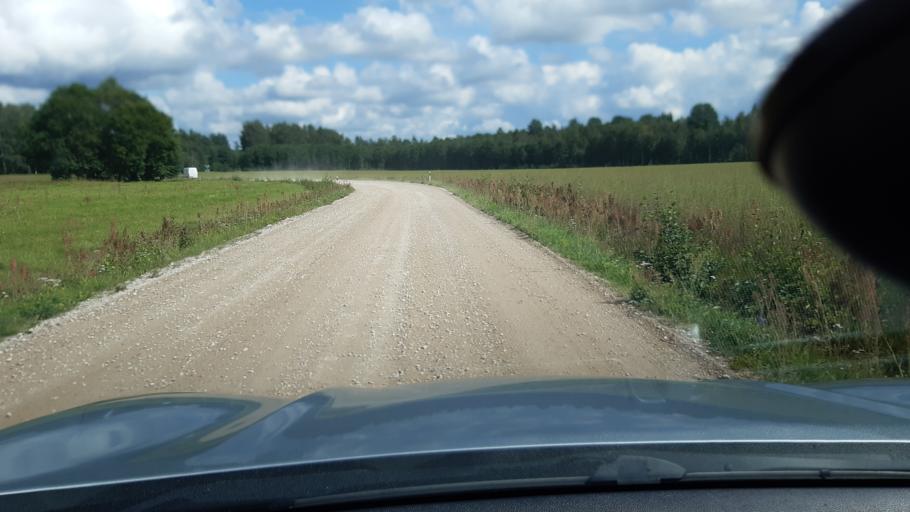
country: EE
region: Raplamaa
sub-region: Kehtna vald
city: Kehtna
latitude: 58.9087
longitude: 25.1448
